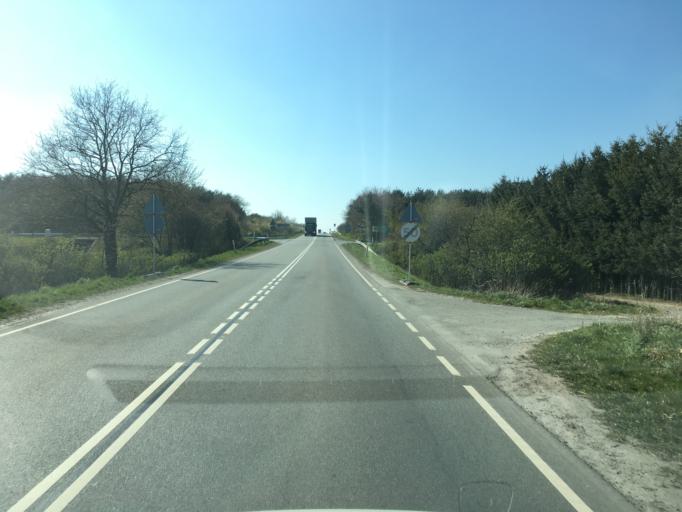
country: DK
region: South Denmark
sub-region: Aabenraa Kommune
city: Krusa
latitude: 54.9393
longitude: 9.3872
